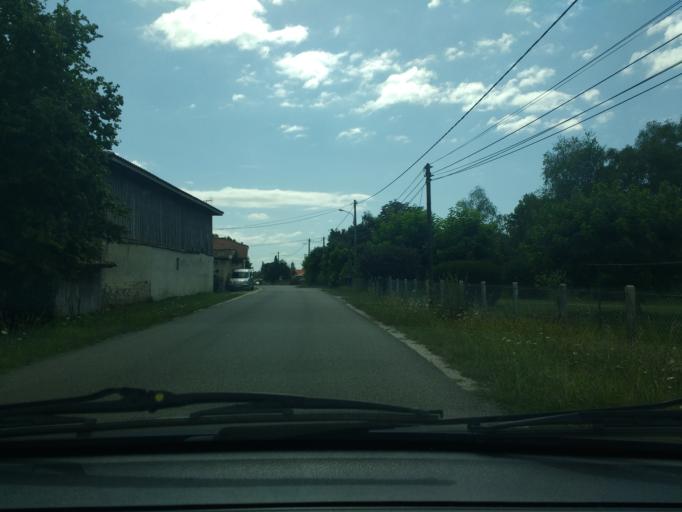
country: FR
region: Aquitaine
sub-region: Departement de la Gironde
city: Salles
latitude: 44.5600
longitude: -0.8511
